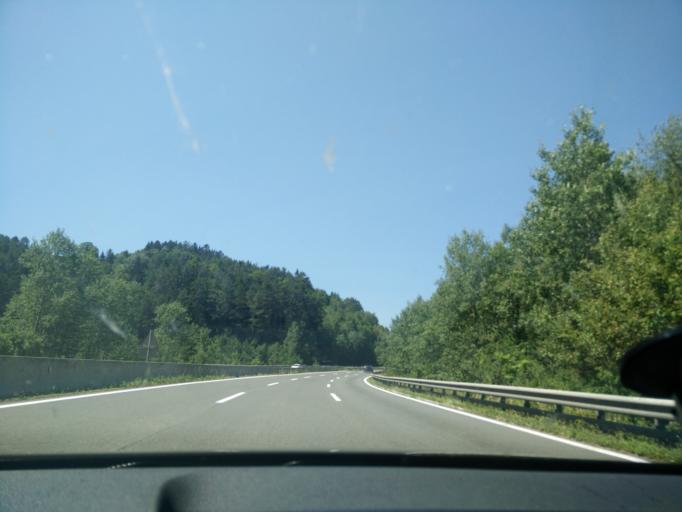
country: AT
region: Lower Austria
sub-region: Politischer Bezirk Neunkirchen
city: Edlitz
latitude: 47.5907
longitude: 16.1172
